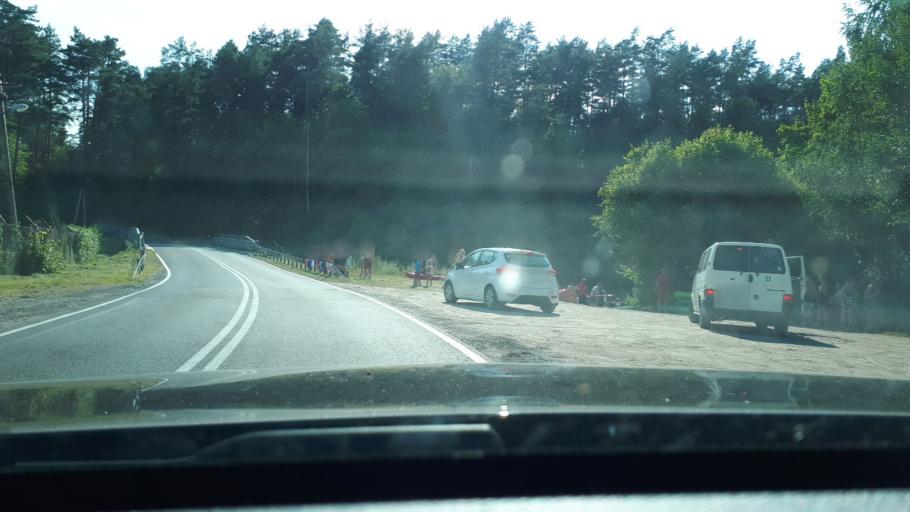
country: PL
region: Warmian-Masurian Voivodeship
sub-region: Powiat olsztynski
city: Stawiguda
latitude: 53.5373
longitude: 20.4637
